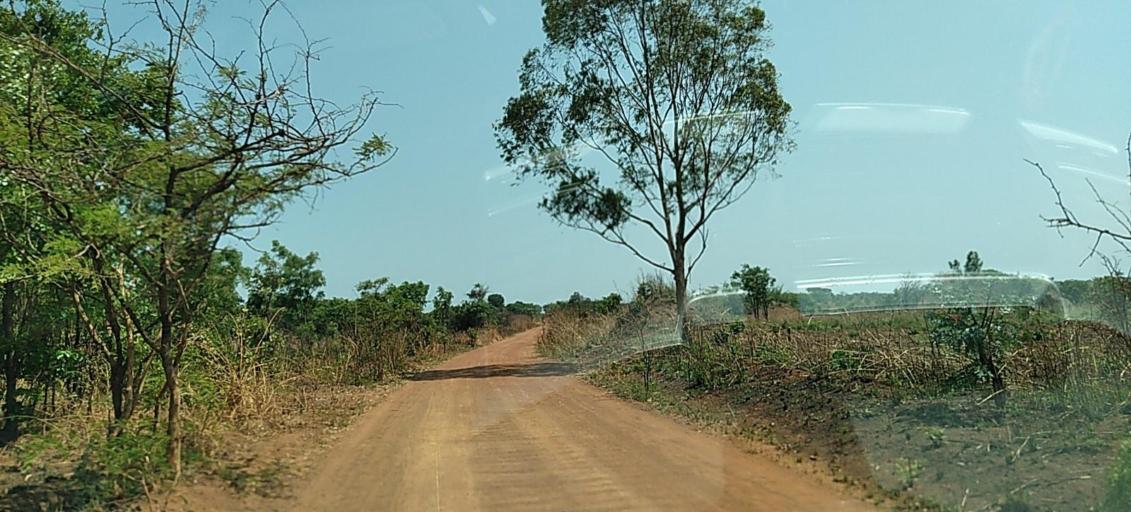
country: ZM
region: Copperbelt
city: Chingola
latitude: -12.5329
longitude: 27.7222
